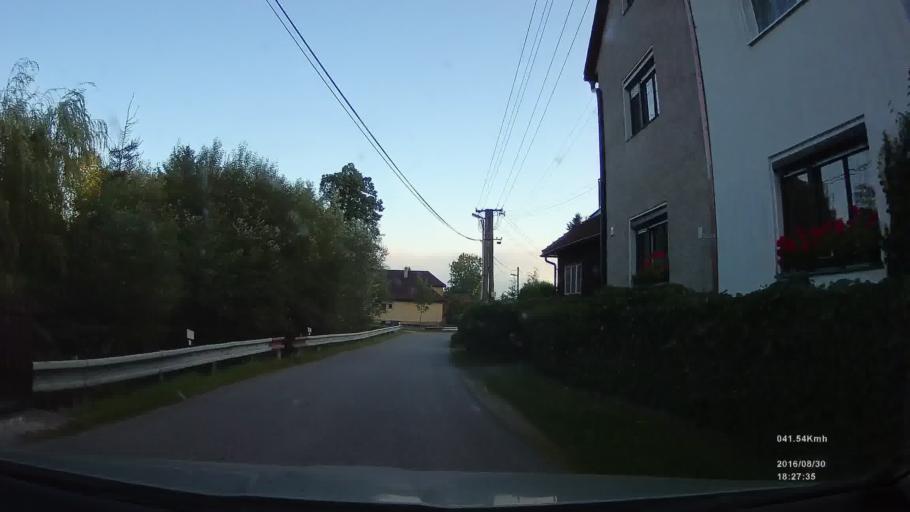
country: SK
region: Zilinsky
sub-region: Okres Liptovsky Mikulas
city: Liptovsky Mikulas
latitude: 49.1464
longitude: 19.5012
